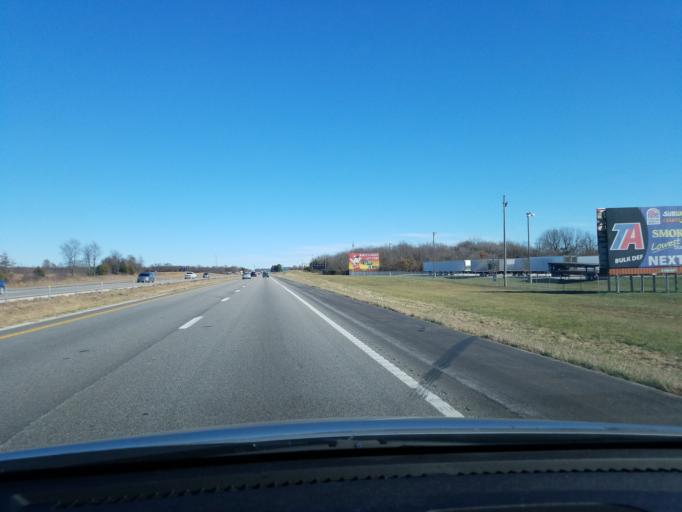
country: US
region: Missouri
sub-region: Greene County
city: Strafford
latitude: 37.2575
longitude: -93.1609
